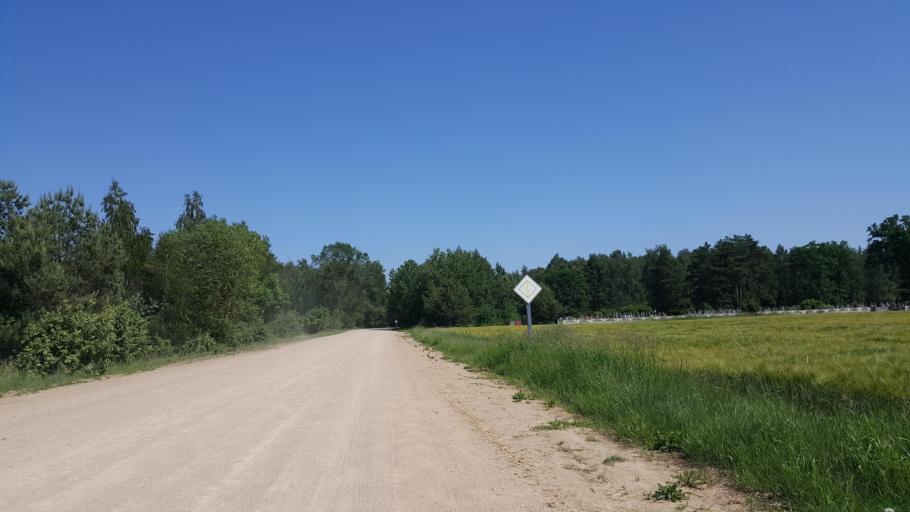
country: BY
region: Brest
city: Zhabinka
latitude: 52.2428
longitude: 24.0082
